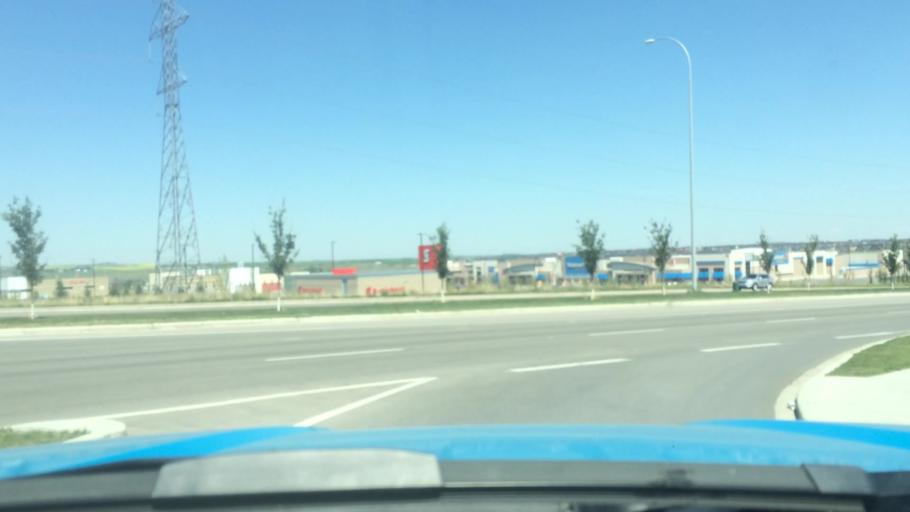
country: CA
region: Alberta
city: Calgary
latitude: 51.1678
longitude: -114.1465
